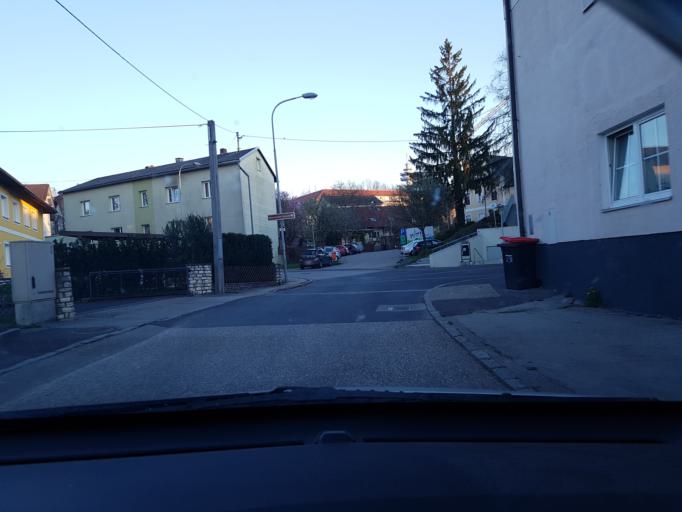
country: AT
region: Upper Austria
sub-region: Politischer Bezirk Linz-Land
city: Ansfelden
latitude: 48.2103
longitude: 14.2911
